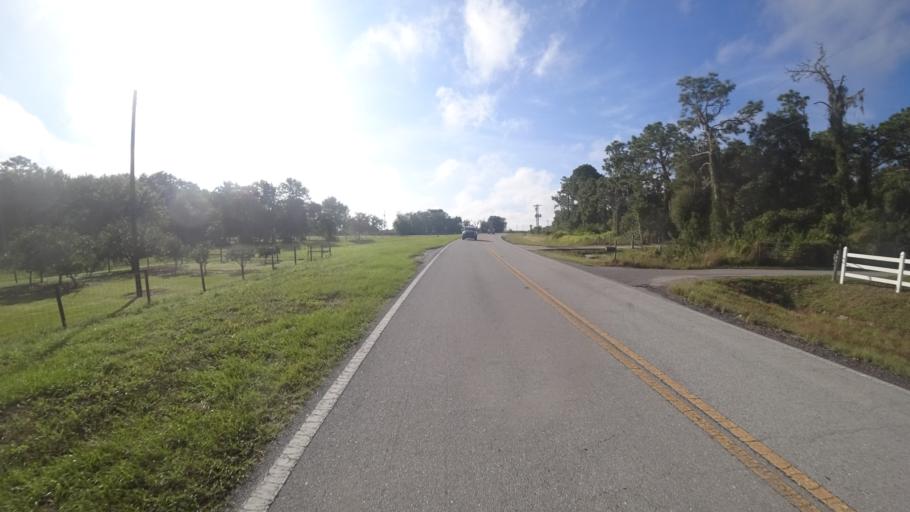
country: US
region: Florida
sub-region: Sarasota County
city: The Meadows
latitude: 27.4681
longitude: -82.3035
